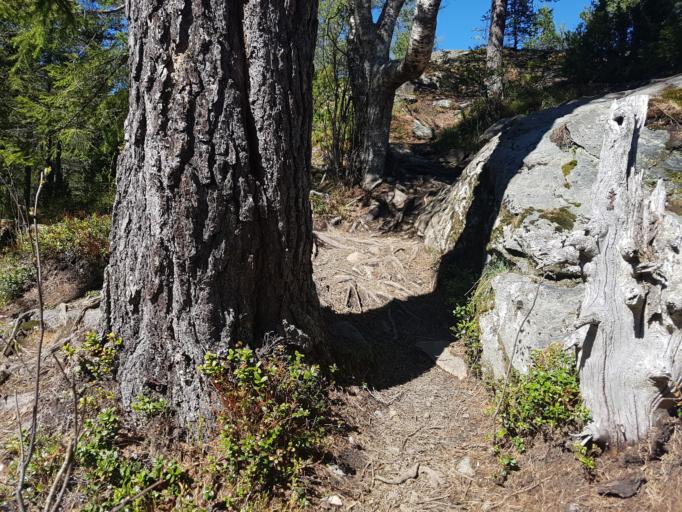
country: NO
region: Sor-Trondelag
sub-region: Trondheim
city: Trondheim
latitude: 63.4365
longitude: 10.3347
